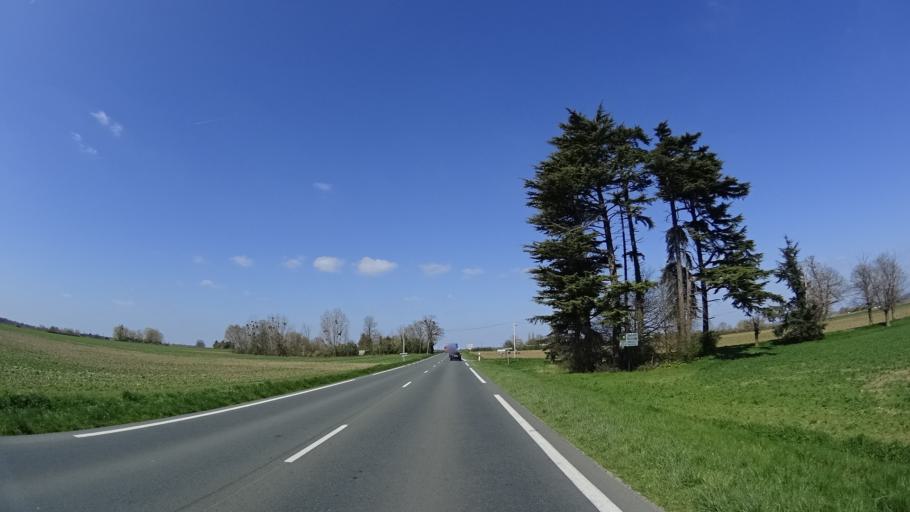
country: FR
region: Pays de la Loire
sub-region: Departement de Maine-et-Loire
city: Brissac-Quince
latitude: 47.3325
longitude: -0.4241
